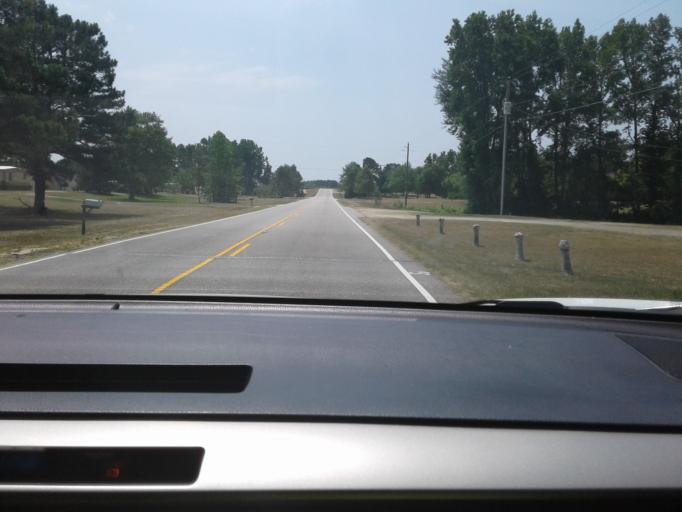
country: US
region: North Carolina
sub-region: Harnett County
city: Coats
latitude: 35.4562
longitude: -78.6898
